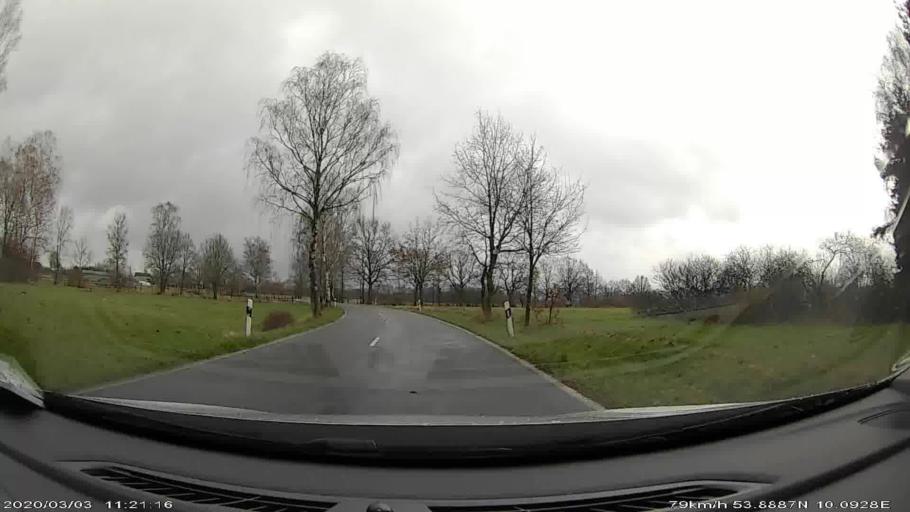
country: DE
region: Schleswig-Holstein
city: Hartenholm
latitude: 53.8883
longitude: 10.0976
